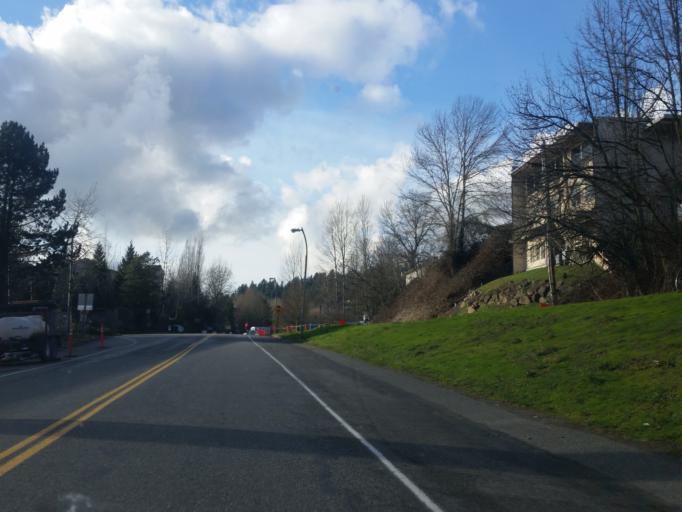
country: US
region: Washington
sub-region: King County
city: Kenmore
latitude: 47.7580
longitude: -122.2597
